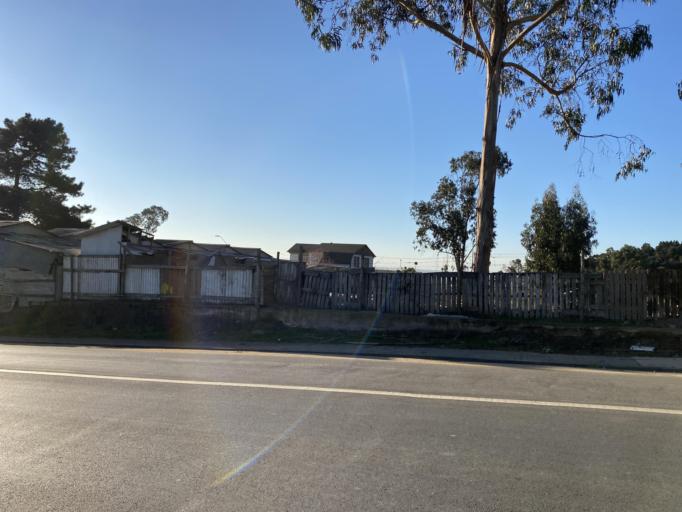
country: CL
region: Valparaiso
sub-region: San Antonio Province
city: Cartagena
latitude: -33.5503
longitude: -71.5899
